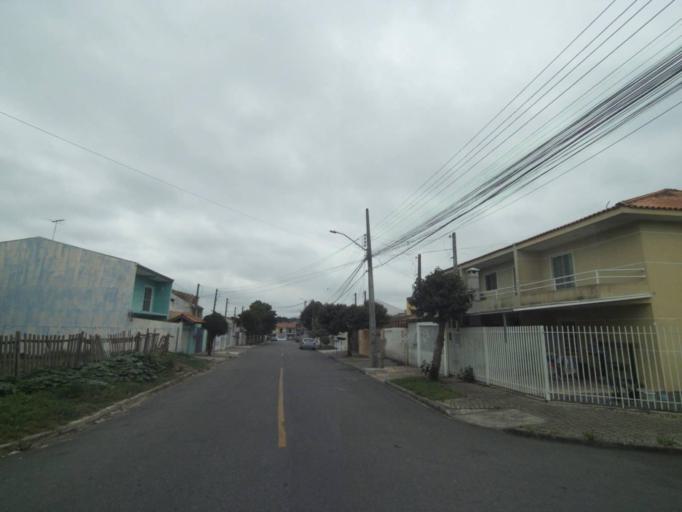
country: BR
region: Parana
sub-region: Araucaria
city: Araucaria
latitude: -25.5454
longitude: -49.3386
